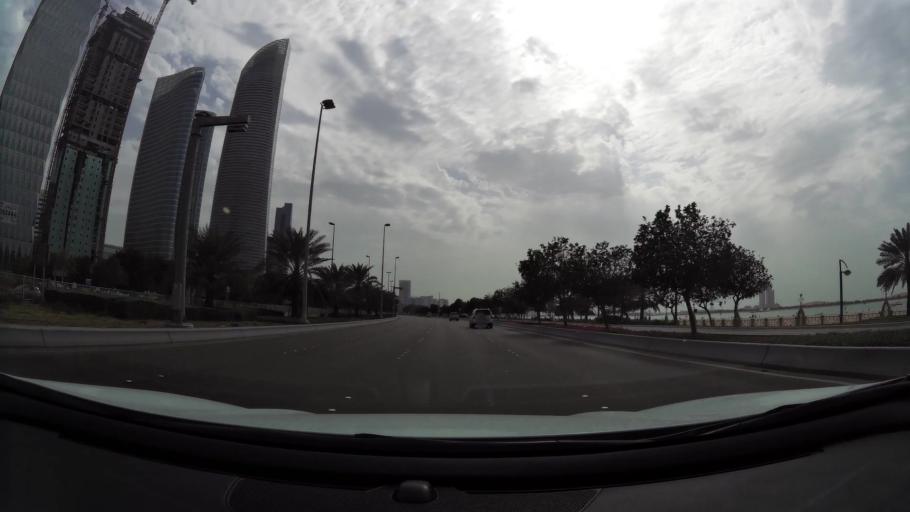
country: AE
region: Abu Dhabi
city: Abu Dhabi
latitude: 24.4894
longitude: 54.3510
